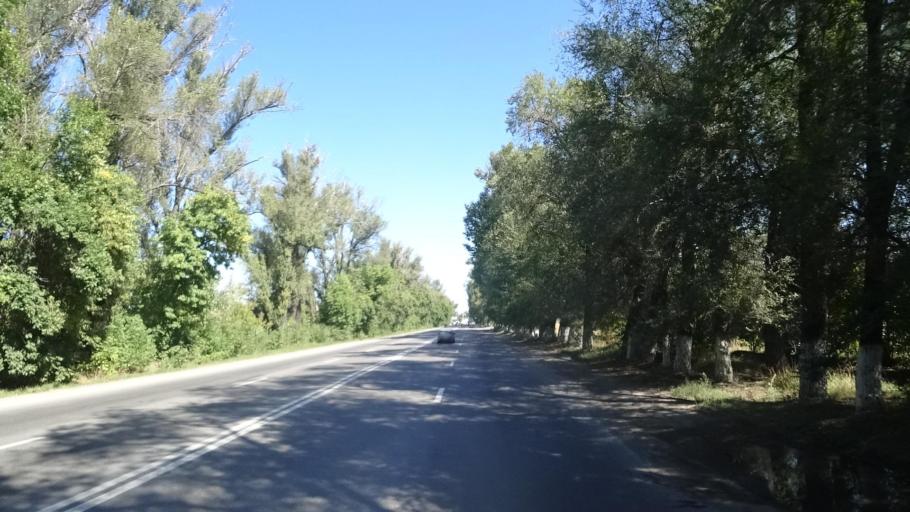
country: KZ
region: Almaty Oblysy
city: Energeticheskiy
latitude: 43.3314
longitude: 77.0356
